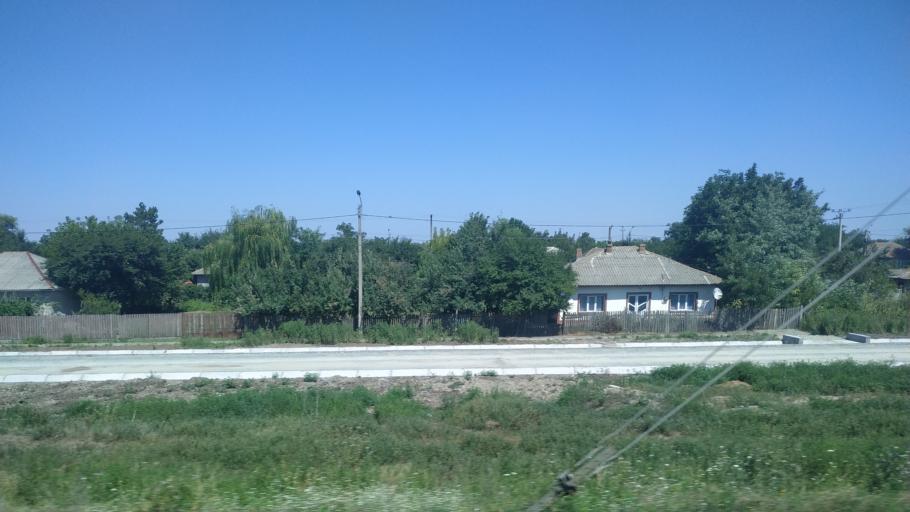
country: RO
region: Calarasi
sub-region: Comuna Perisoru
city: Perisoru
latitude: 44.4213
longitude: 27.6437
